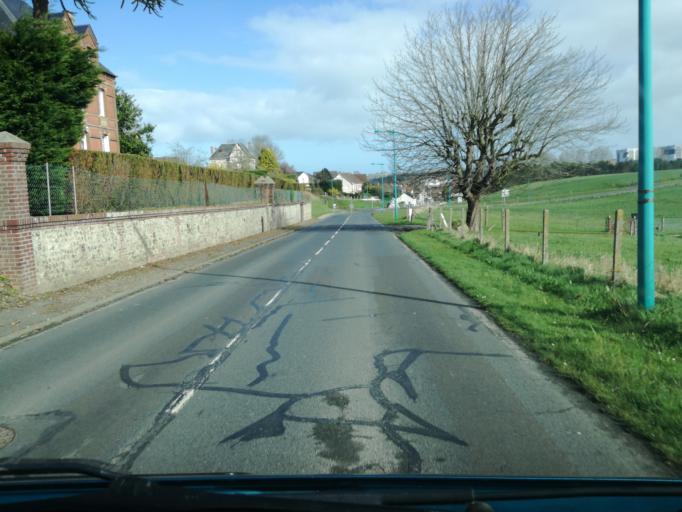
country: FR
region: Haute-Normandie
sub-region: Departement de la Seine-Maritime
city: Saint-Leonard
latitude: 49.7422
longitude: 0.3615
